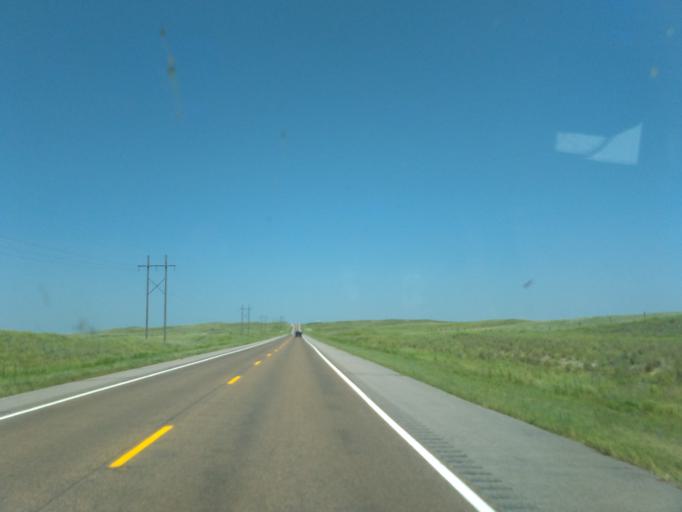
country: US
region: Nebraska
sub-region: Lincoln County
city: North Platte
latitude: 40.8624
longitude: -100.7541
